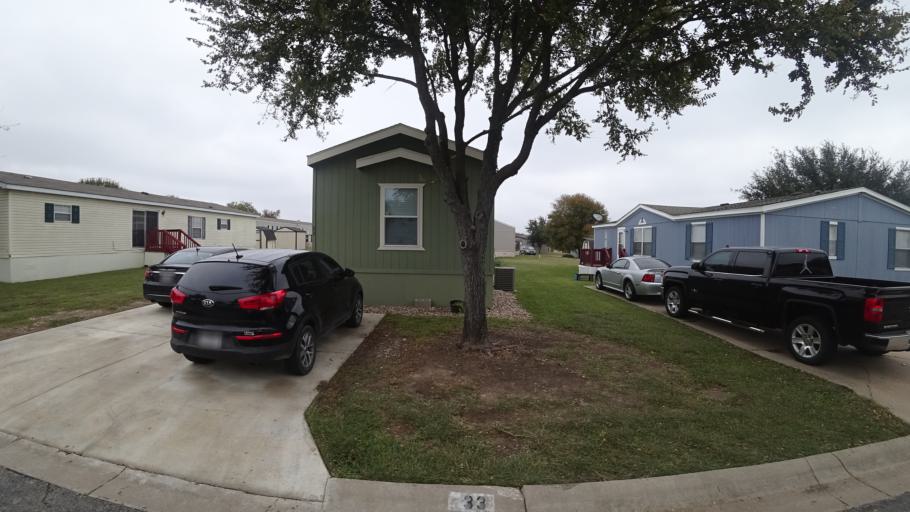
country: US
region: Texas
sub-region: Travis County
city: Pflugerville
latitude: 30.4135
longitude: -97.6065
